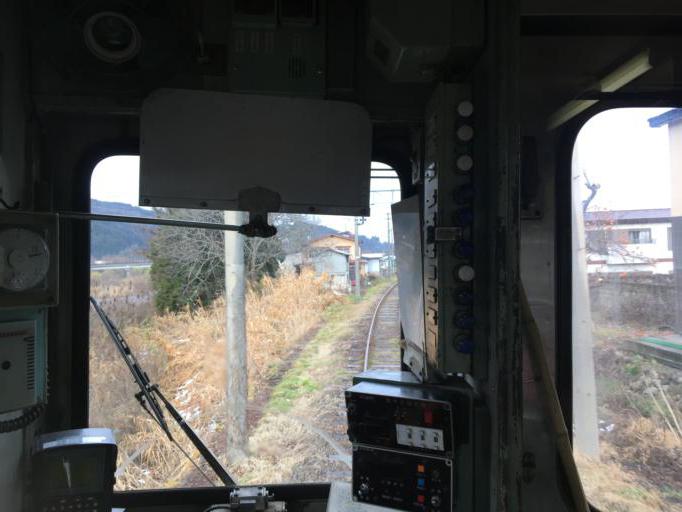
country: JP
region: Aomori
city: Hirosaki
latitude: 40.5240
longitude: 140.5584
